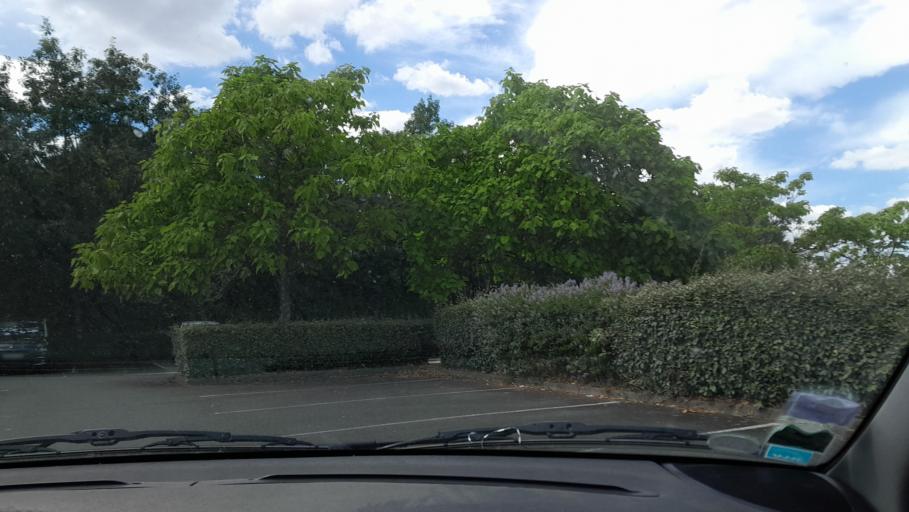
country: FR
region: Pays de la Loire
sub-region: Departement de la Mayenne
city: Laval
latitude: 48.0904
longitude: -0.7633
